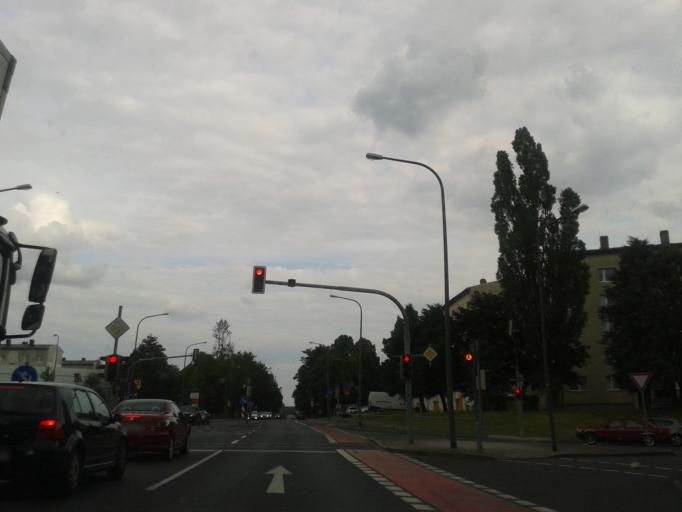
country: DE
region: Saxony
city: Albertstadt
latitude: 51.1189
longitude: 13.7661
